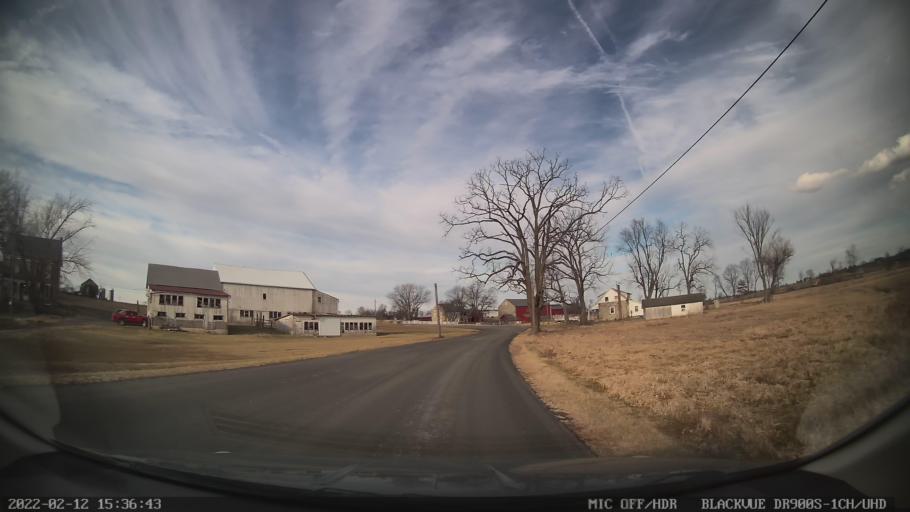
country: US
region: Pennsylvania
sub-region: Berks County
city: Topton
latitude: 40.4936
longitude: -75.7371
